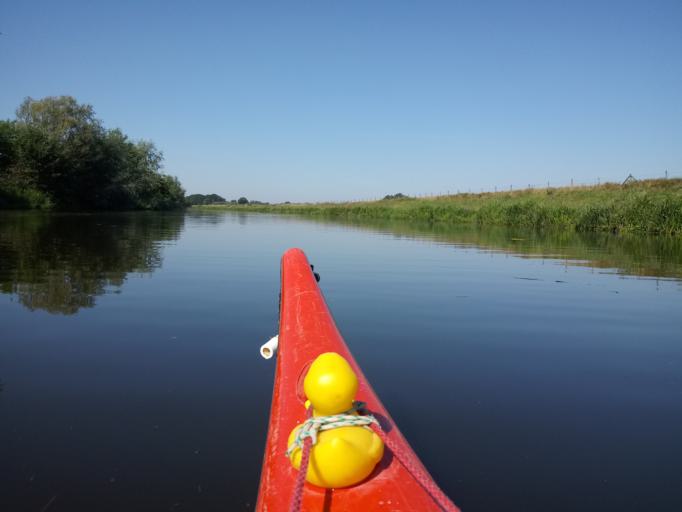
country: NL
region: Gelderland
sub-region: Berkelland
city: Eibergen
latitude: 52.1061
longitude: 6.6890
